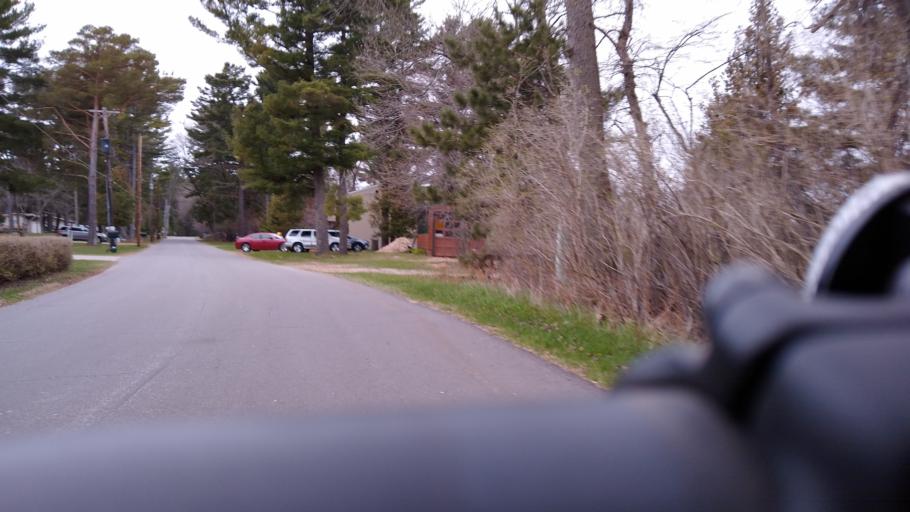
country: US
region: Michigan
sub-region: Delta County
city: Escanaba
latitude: 45.7022
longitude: -87.0953
